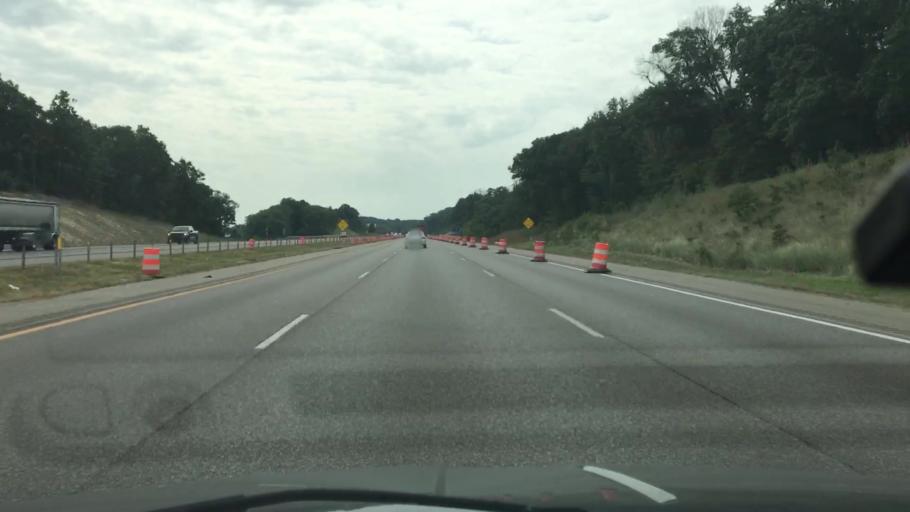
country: US
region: Michigan
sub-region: Berrien County
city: Bridgman
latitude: 41.9461
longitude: -86.5653
